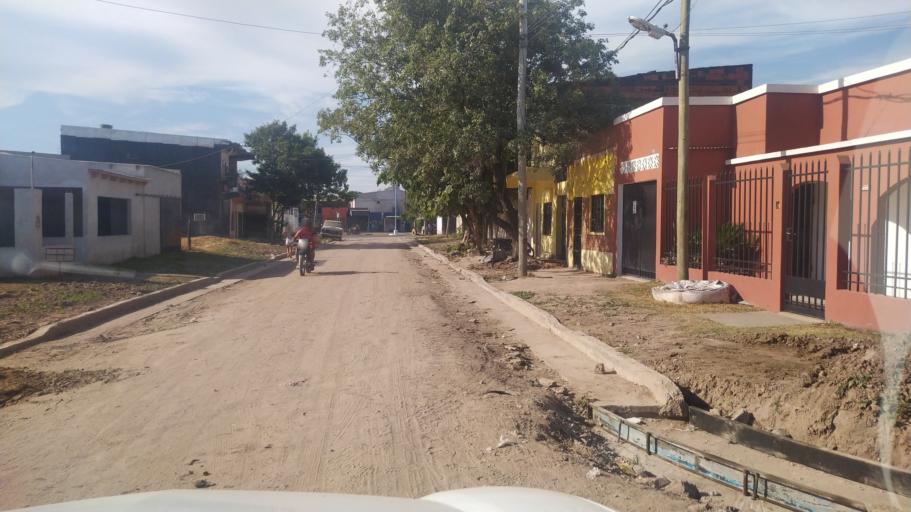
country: AR
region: Corrientes
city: Corrientes
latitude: -27.4881
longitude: -58.8114
